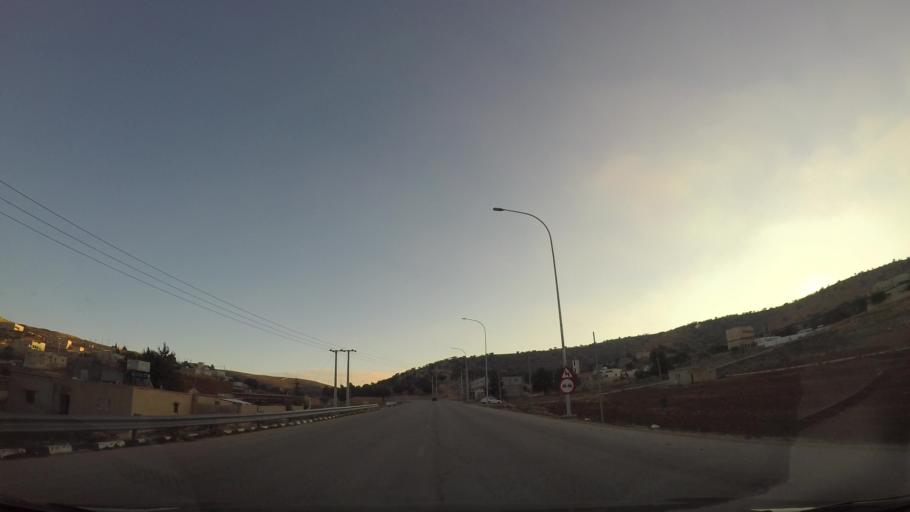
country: JO
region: Ma'an
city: Petra
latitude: 30.4167
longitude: 35.5089
